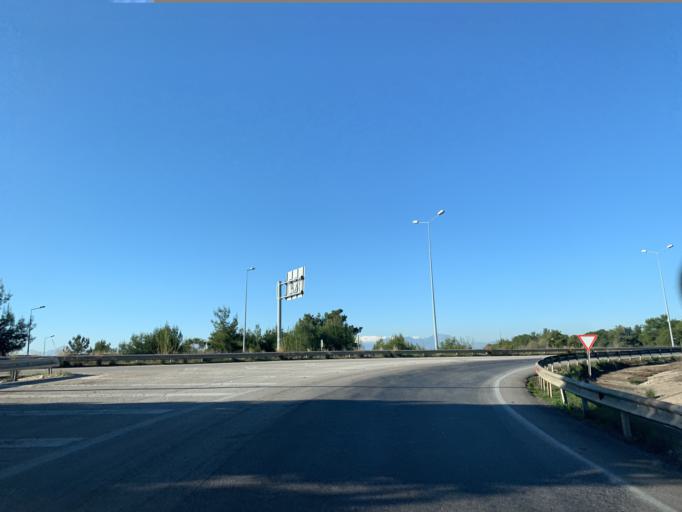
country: TR
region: Antalya
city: Aksu
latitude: 36.9446
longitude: 30.8325
